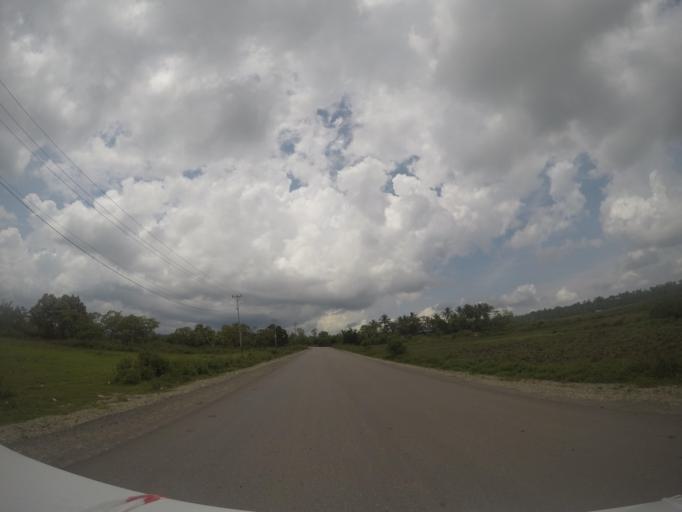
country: TL
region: Baucau
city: Venilale
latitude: -8.5556
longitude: 126.4050
